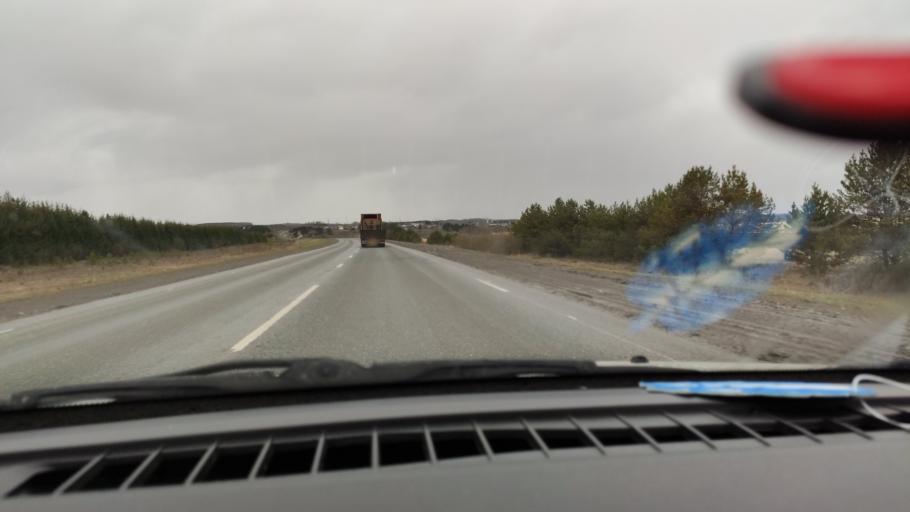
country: RU
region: Perm
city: Kungur
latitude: 57.3623
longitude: 56.9277
